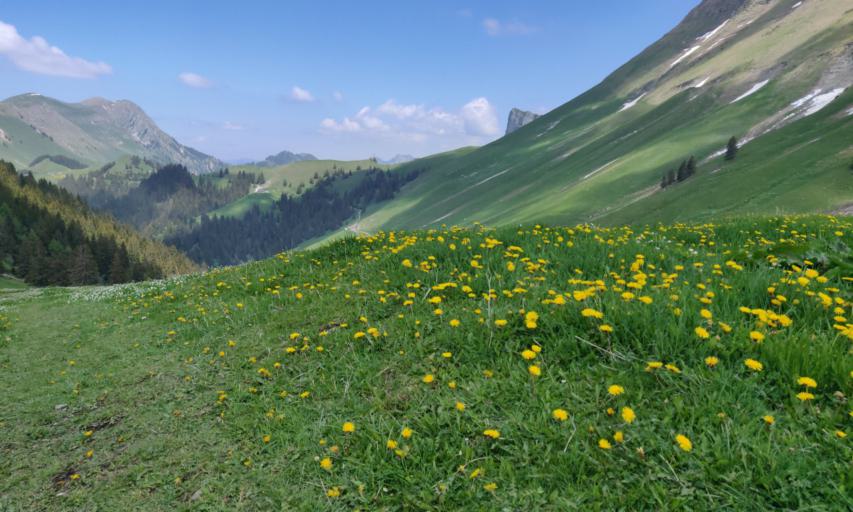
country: CH
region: Vaud
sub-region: Riviera-Pays-d'Enhaut District
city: Caux
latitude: 46.5050
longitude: 6.9844
